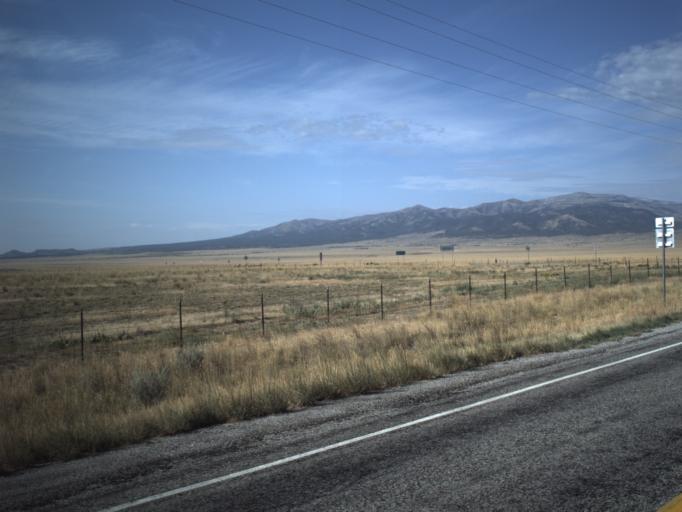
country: US
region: Idaho
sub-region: Oneida County
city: Malad City
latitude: 41.9654
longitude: -113.0594
